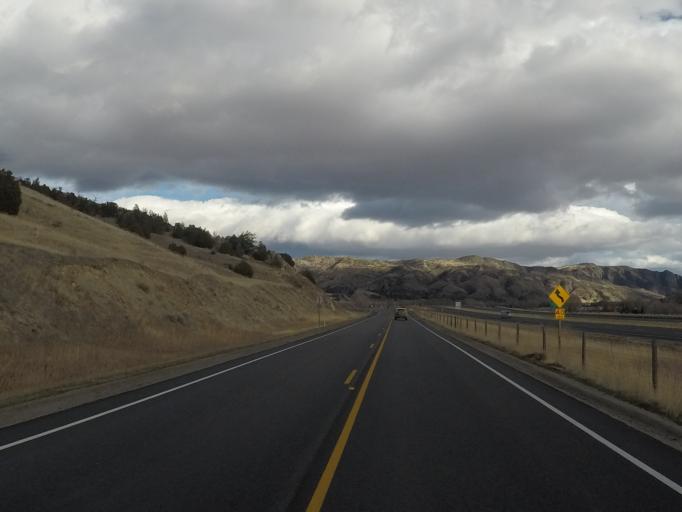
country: US
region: Montana
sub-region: Jefferson County
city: Whitehall
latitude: 45.8714
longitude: -111.9631
